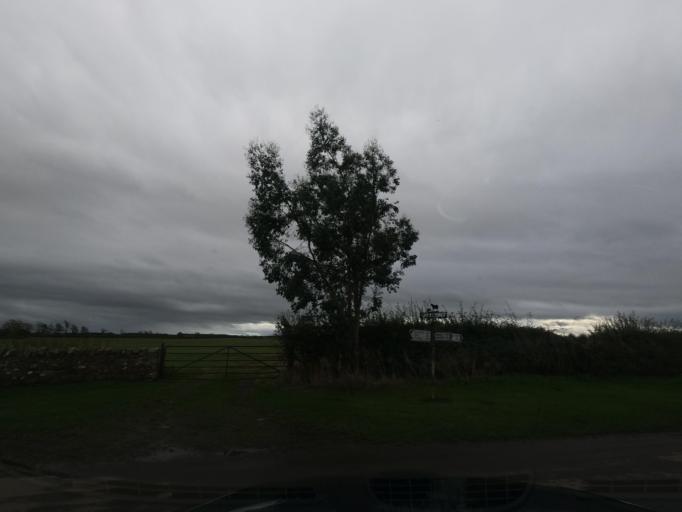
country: GB
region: England
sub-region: Northumberland
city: Ford
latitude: 55.6919
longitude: -2.0864
